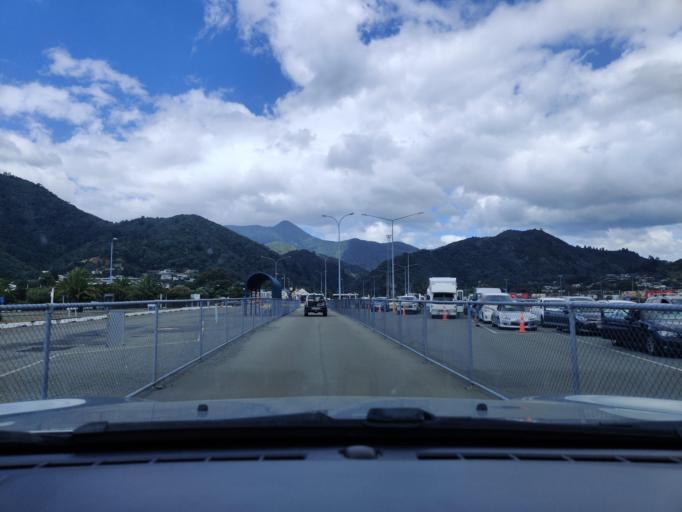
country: NZ
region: Marlborough
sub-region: Marlborough District
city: Picton
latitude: -41.2861
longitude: 174.0044
